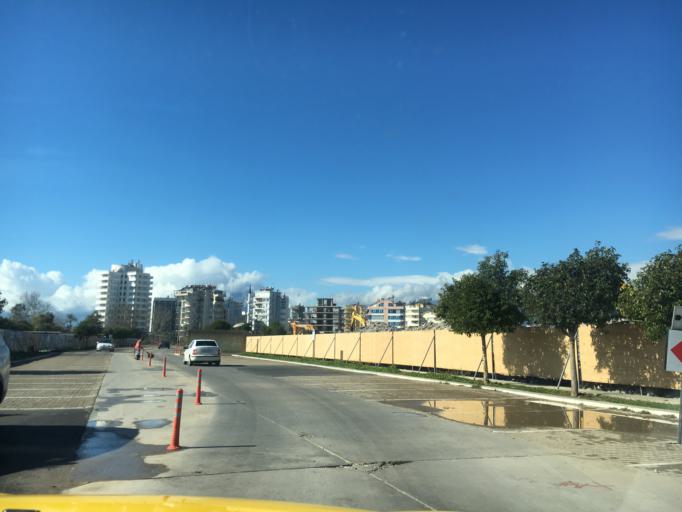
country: TR
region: Antalya
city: Antalya
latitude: 36.8765
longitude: 30.6597
